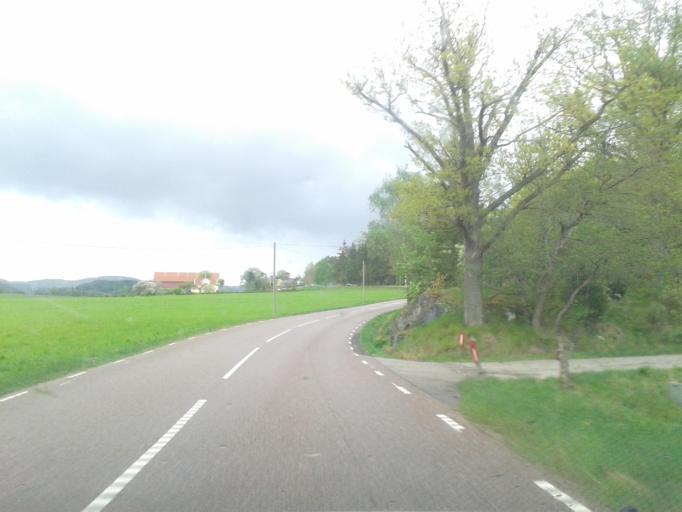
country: SE
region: Vaestra Goetaland
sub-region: Lilla Edets Kommun
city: Lilla Edet
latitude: 58.1061
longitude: 12.1161
